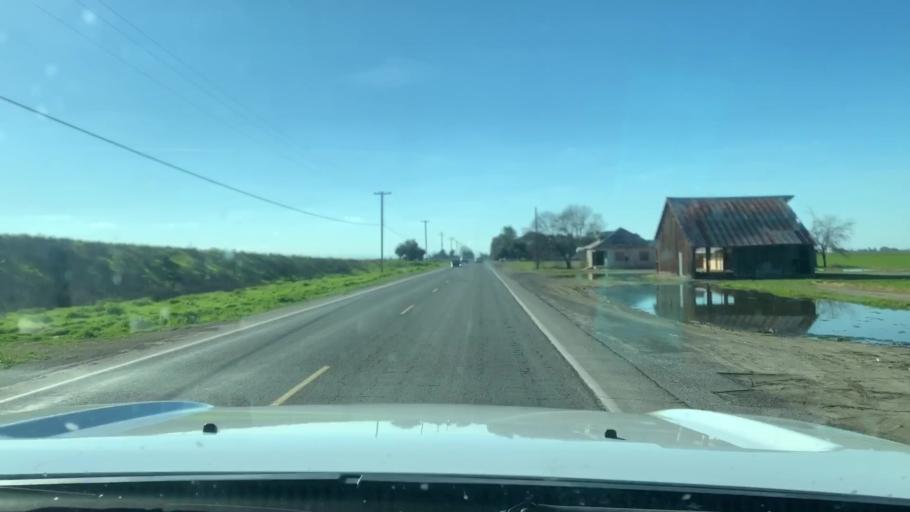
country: US
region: California
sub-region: Kings County
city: Home Garden
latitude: 36.2111
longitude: -119.6142
